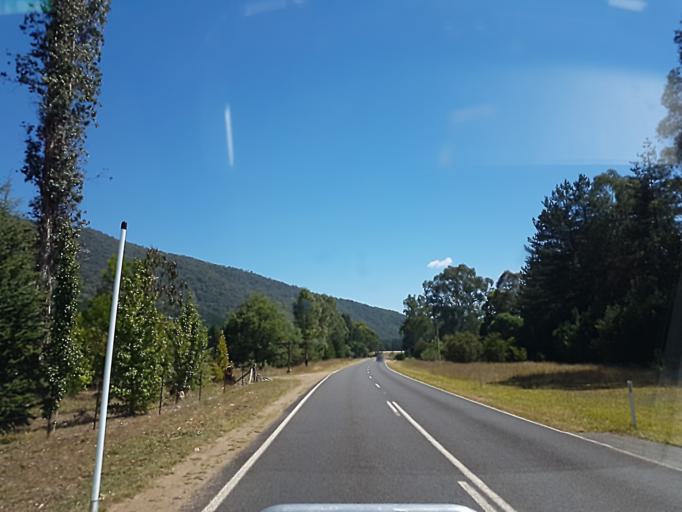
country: AU
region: Victoria
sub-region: Alpine
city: Mount Beauty
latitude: -36.7677
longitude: 147.0258
